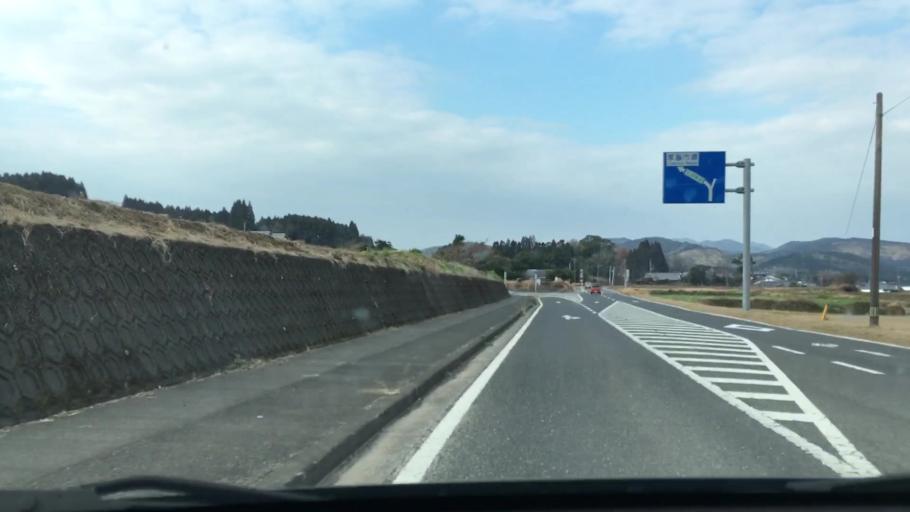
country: JP
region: Miyazaki
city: Kushima
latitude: 31.5189
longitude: 131.2380
